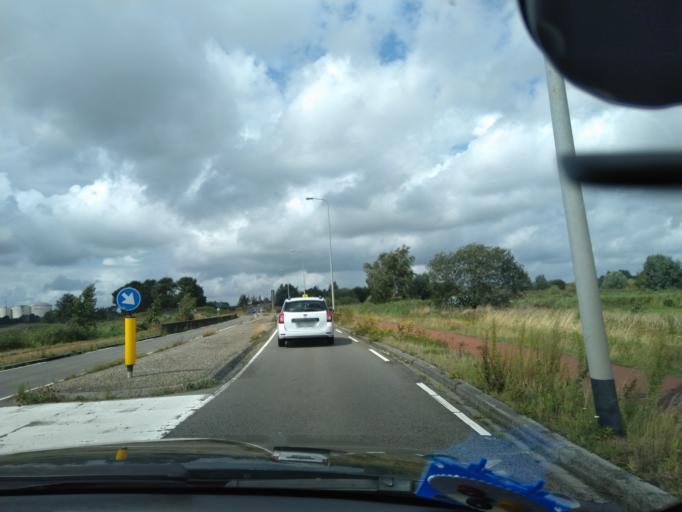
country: NL
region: Groningen
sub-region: Gemeente Groningen
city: Groningen
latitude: 53.2048
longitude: 6.5180
